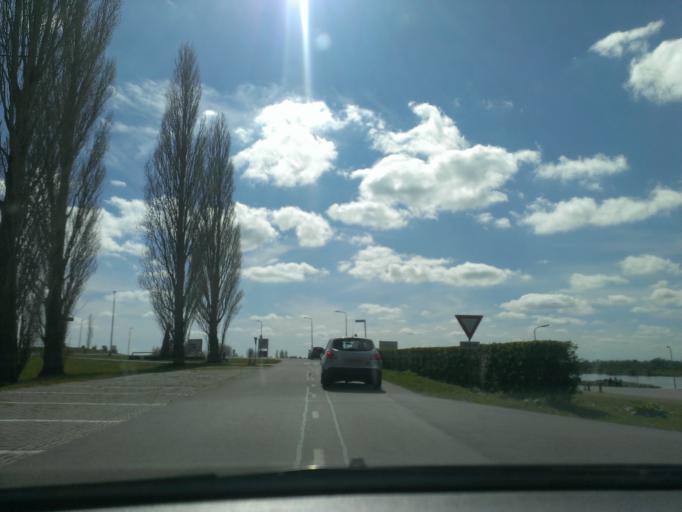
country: NL
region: Overijssel
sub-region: Gemeente Olst-Wijhe
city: Wijhe
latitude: 52.3865
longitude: 6.1284
